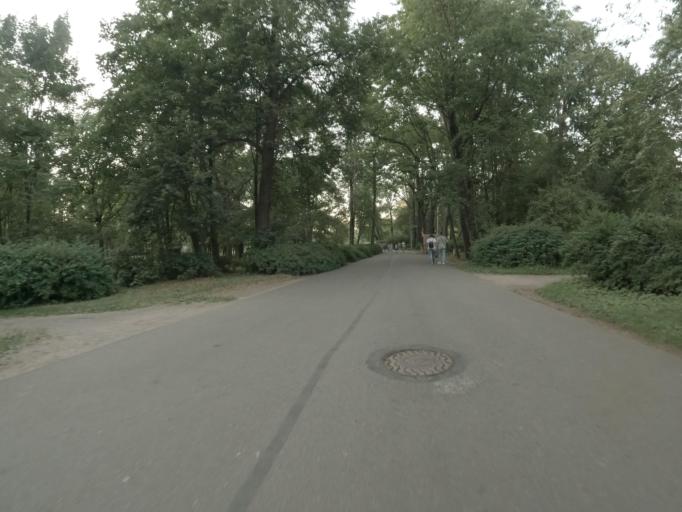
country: RU
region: Leningrad
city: Krestovskiy ostrov
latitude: 59.9798
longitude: 30.2539
